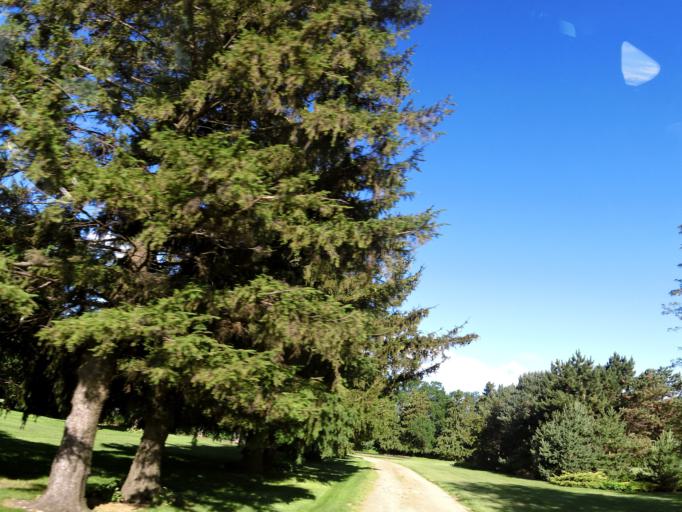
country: US
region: Minnesota
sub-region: Dakota County
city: Hastings
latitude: 44.8122
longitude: -92.8629
